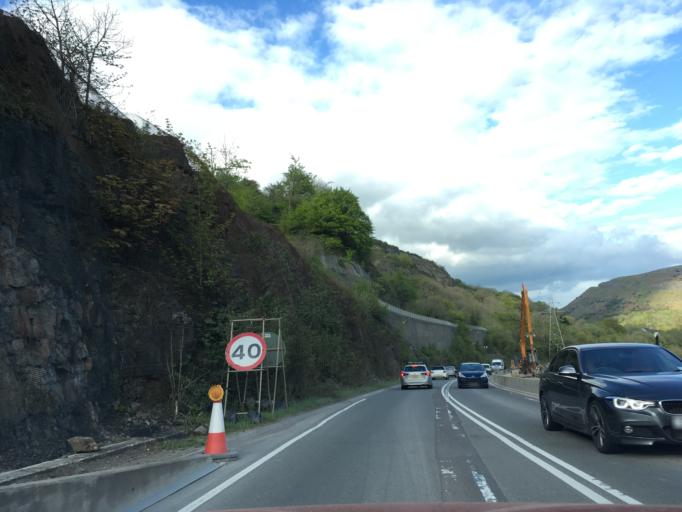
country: GB
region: Wales
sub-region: Blaenau Gwent
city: Brynmawr
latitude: 51.8070
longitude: -3.1374
